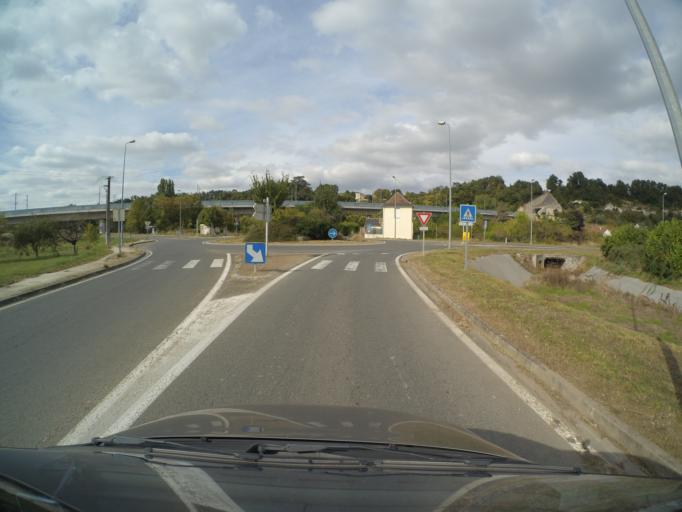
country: FR
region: Centre
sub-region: Departement d'Indre-et-Loire
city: Vouvray
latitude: 47.4115
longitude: 0.8233
